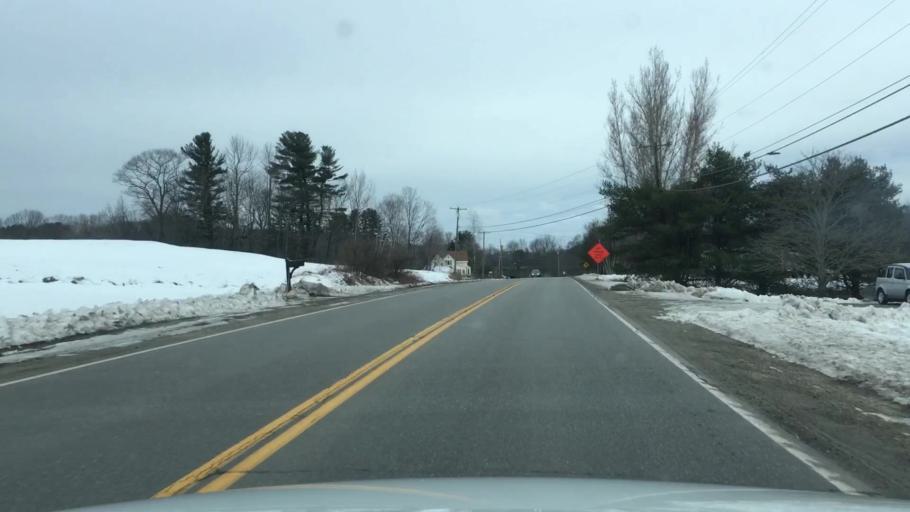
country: US
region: Maine
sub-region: Androscoggin County
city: Lewiston
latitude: 44.0590
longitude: -70.2060
